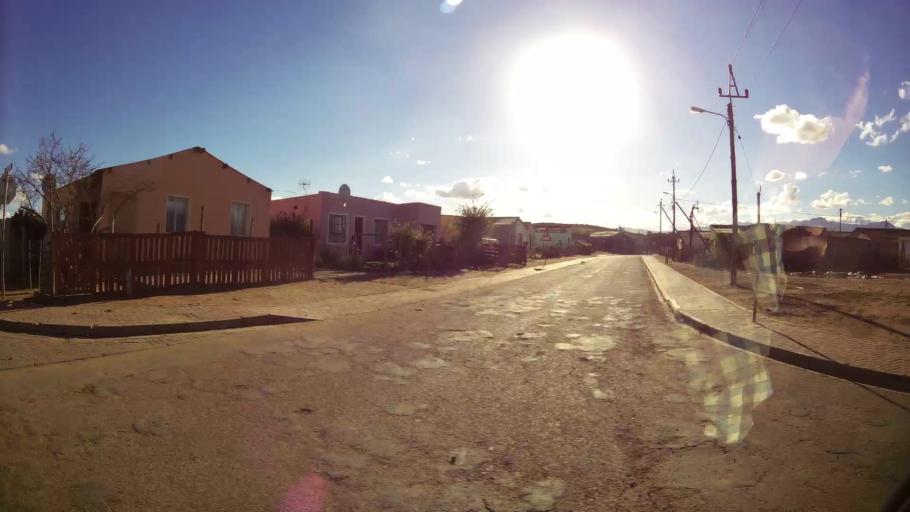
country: ZA
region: Western Cape
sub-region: Eden District Municipality
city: Riversdale
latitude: -34.1081
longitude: 20.9625
